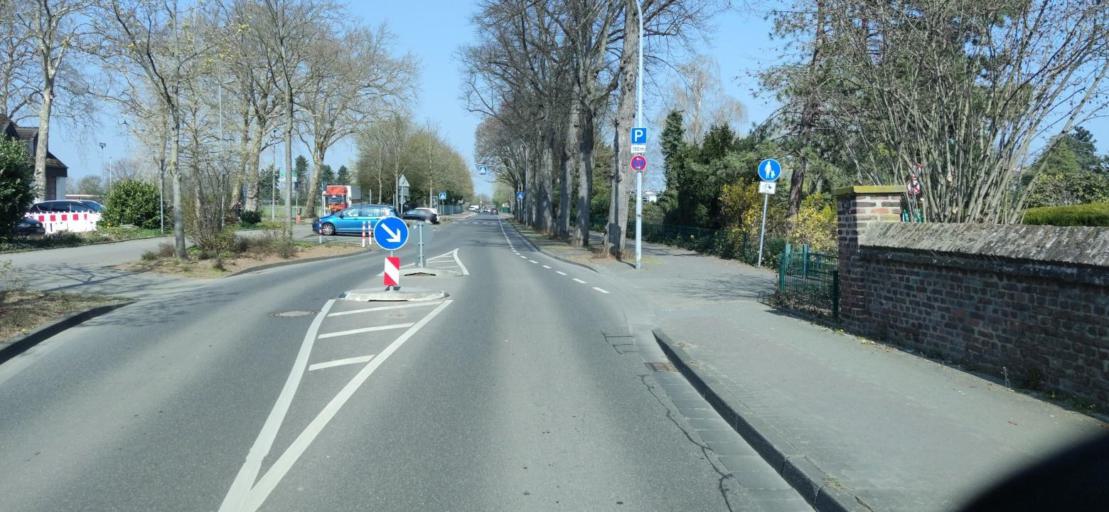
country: DE
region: North Rhine-Westphalia
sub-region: Regierungsbezirk Dusseldorf
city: Kaarst
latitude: 51.2000
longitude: 6.6053
